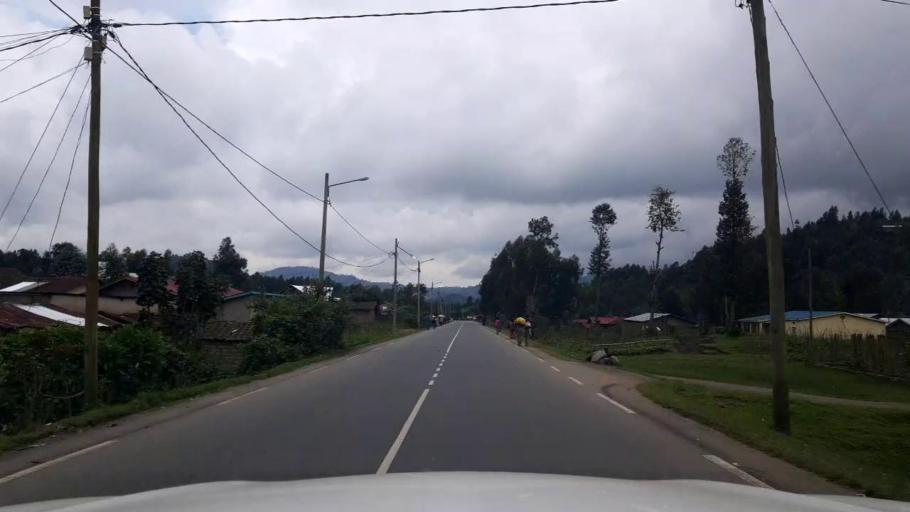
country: RW
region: Northern Province
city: Musanze
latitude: -1.6171
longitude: 29.5024
